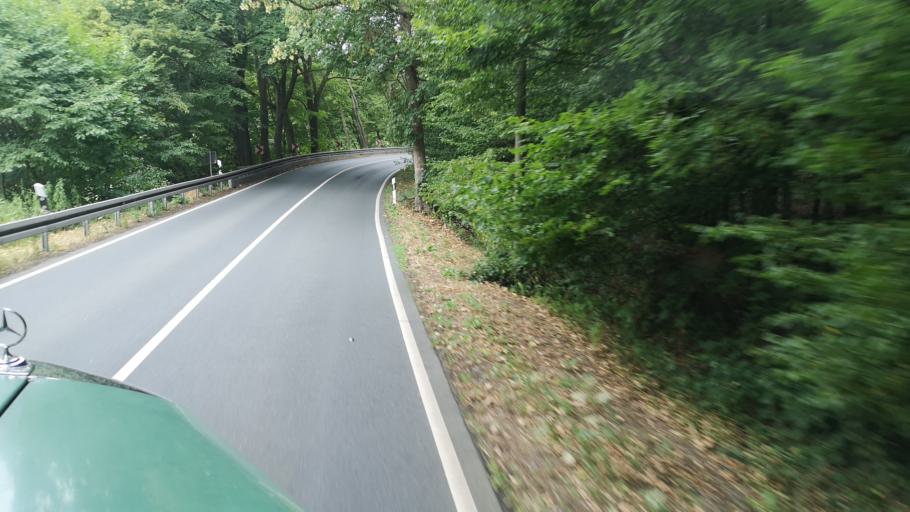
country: DE
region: North Rhine-Westphalia
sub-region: Regierungsbezirk Koln
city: Odenthal
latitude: 51.0660
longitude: 7.1402
